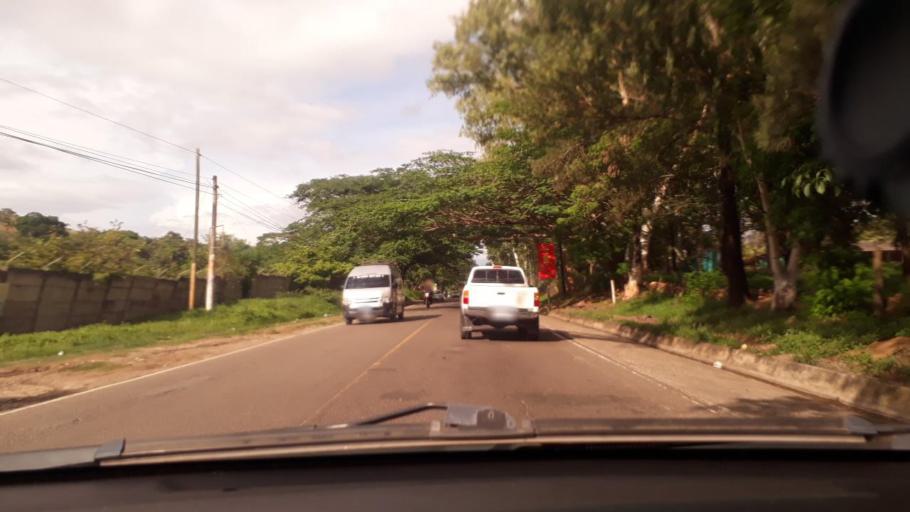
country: GT
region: Jutiapa
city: Jutiapa
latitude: 14.2902
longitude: -89.9283
